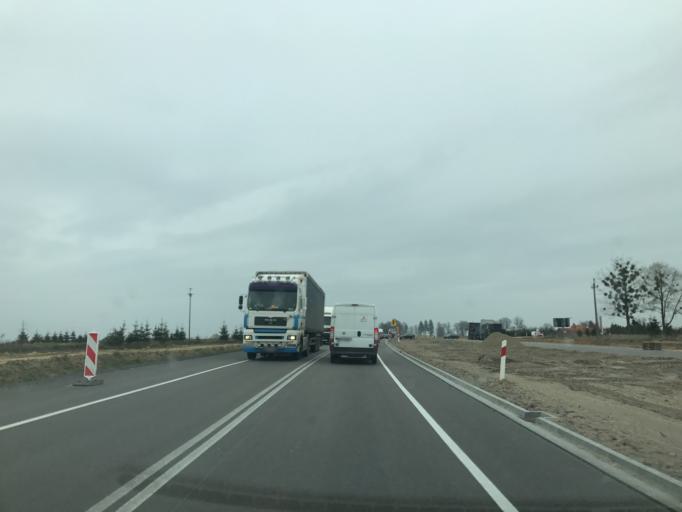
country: PL
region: Warmian-Masurian Voivodeship
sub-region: Powiat olsztynski
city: Olsztynek
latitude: 53.6189
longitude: 20.3360
